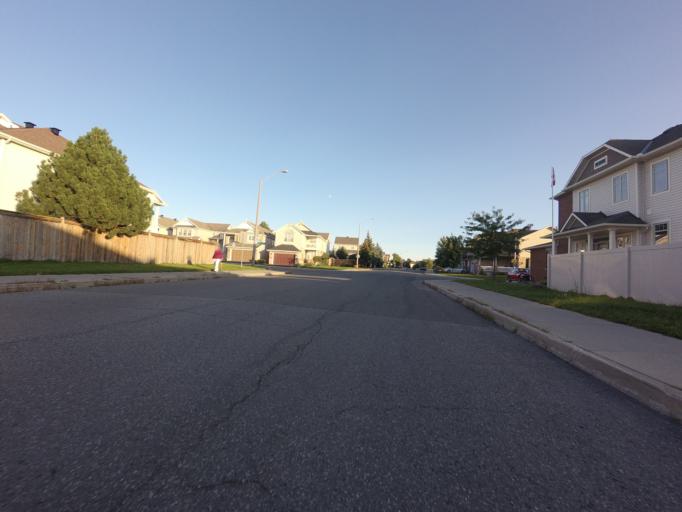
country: CA
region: Ontario
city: Bells Corners
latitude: 45.2791
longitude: -75.7364
